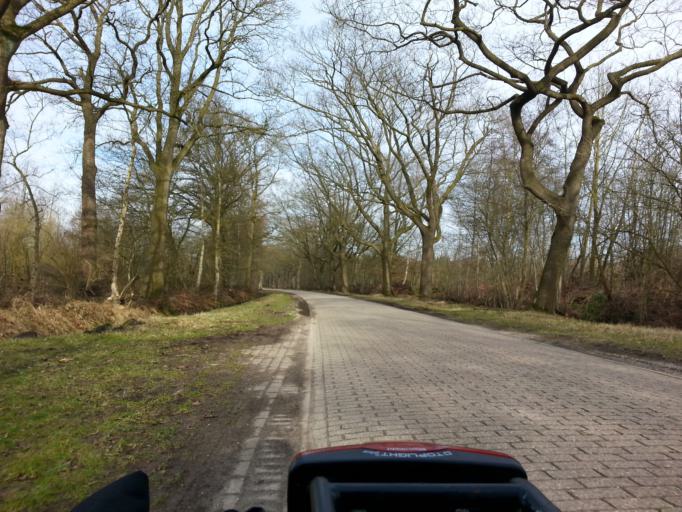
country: NL
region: Utrecht
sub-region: Gemeente Utrechtse Heuvelrug
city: Maarn
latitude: 52.0745
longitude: 5.3852
